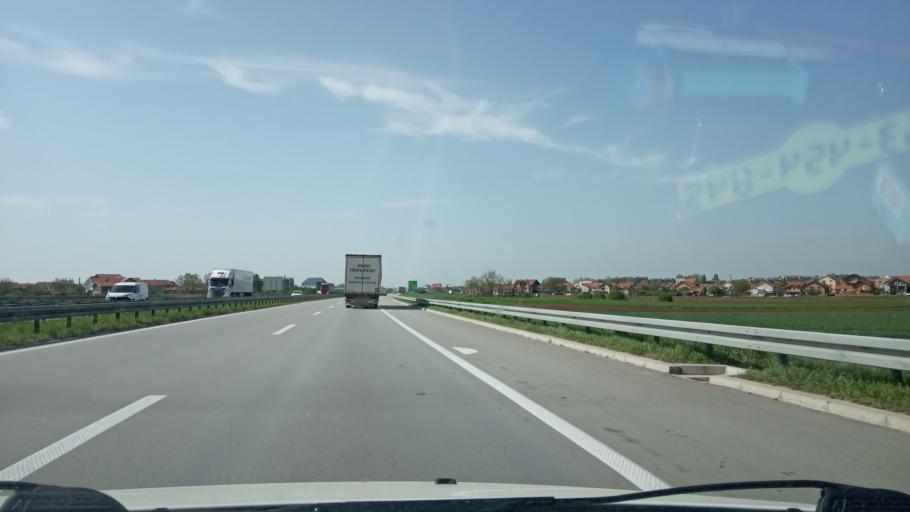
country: RS
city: Novi Banovci
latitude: 44.9028
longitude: 20.3034
